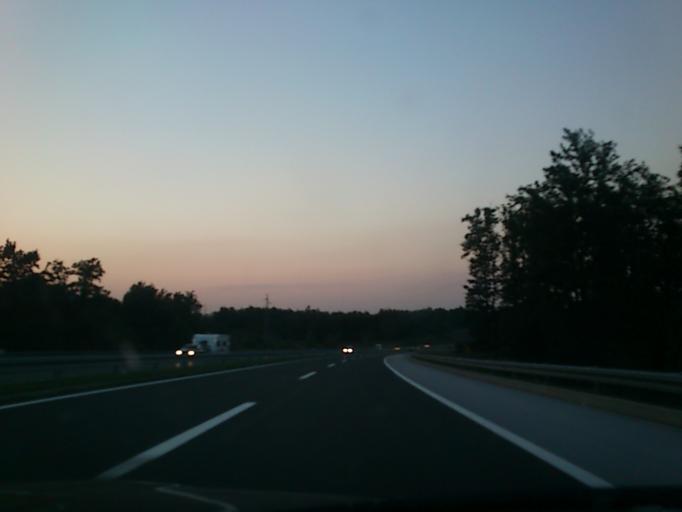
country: HR
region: Karlovacka
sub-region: Grad Ogulin
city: Ogulin
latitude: 45.2884
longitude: 15.2742
